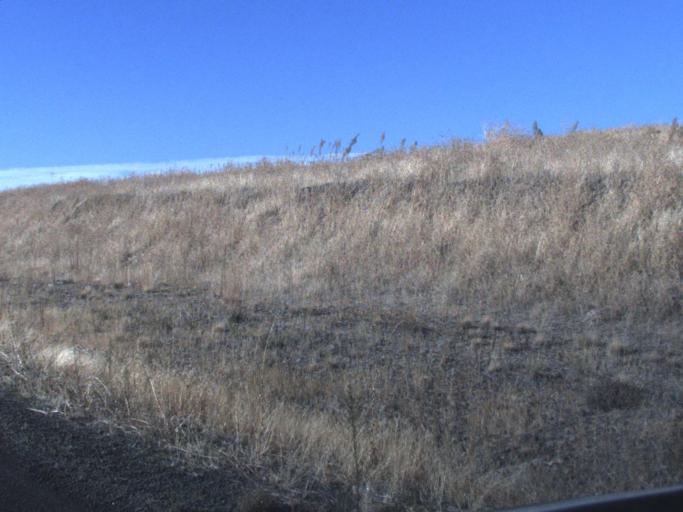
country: US
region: Washington
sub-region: Walla Walla County
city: Walla Walla
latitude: 46.1538
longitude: -118.3750
